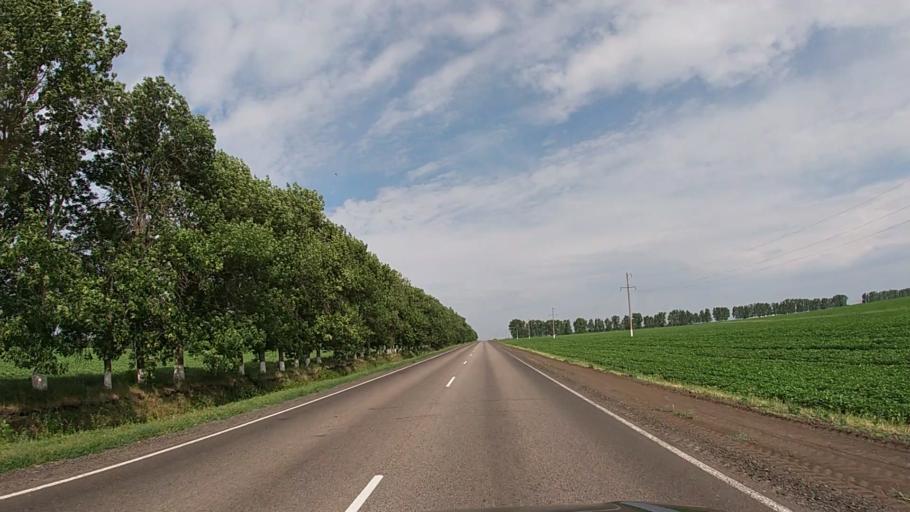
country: RU
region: Belgorod
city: Krasnaya Yaruga
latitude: 50.8033
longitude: 35.5532
